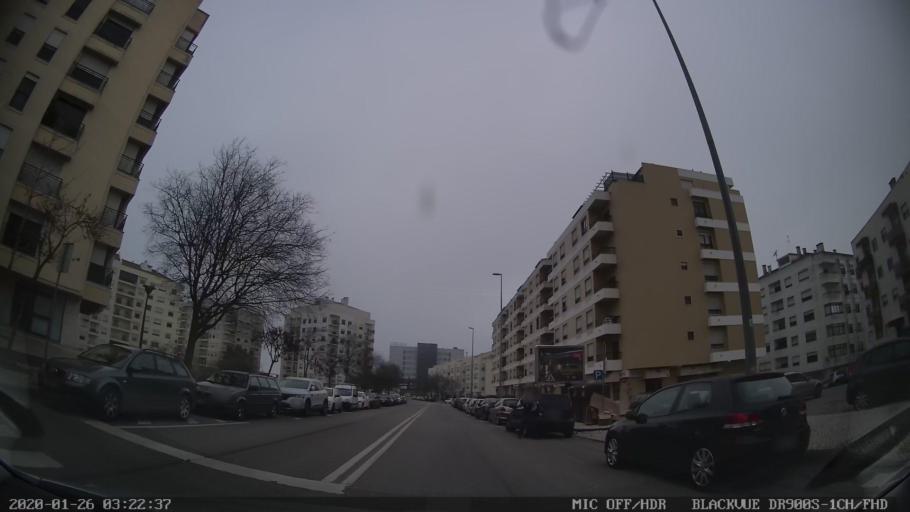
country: PT
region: Santarem
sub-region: Santarem
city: Santarem
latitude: 39.2250
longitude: -8.6907
